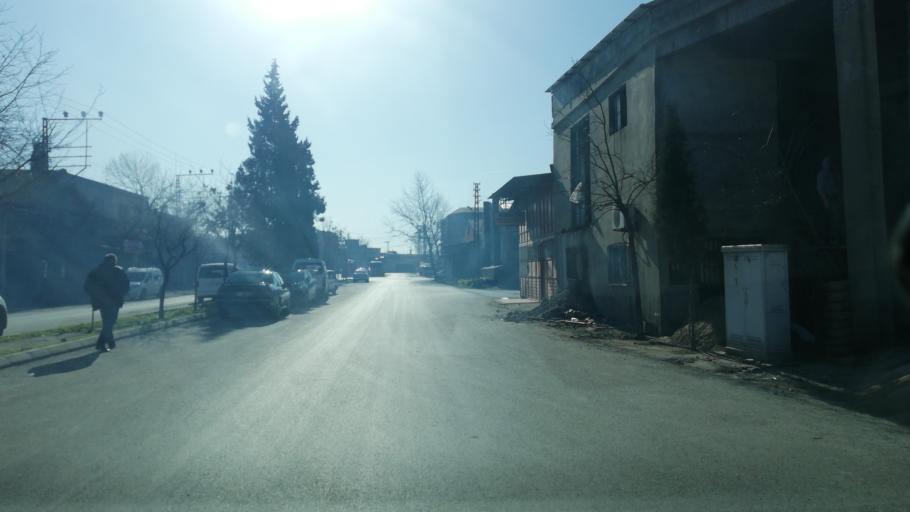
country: TR
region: Kahramanmaras
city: Kahramanmaras
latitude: 37.5596
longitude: 36.9591
